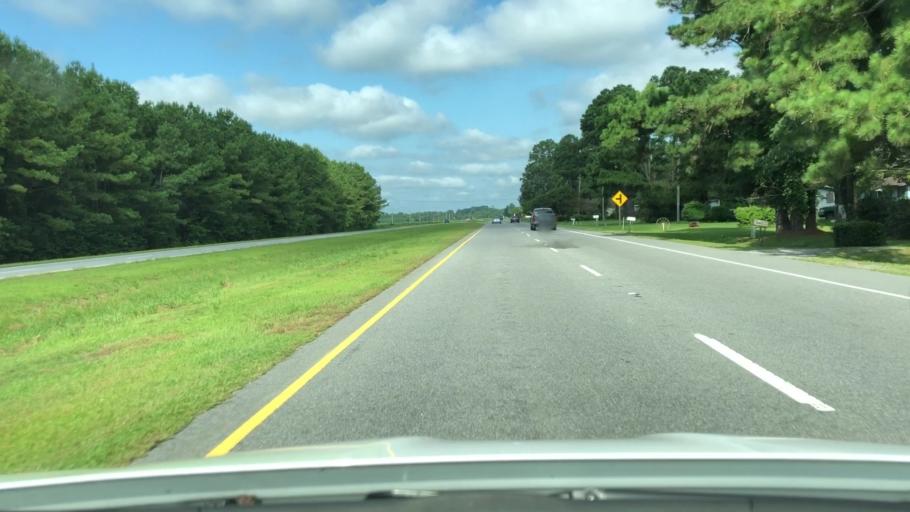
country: US
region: North Carolina
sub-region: Perquimans County
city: Hertford
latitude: 36.2076
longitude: -76.4047
